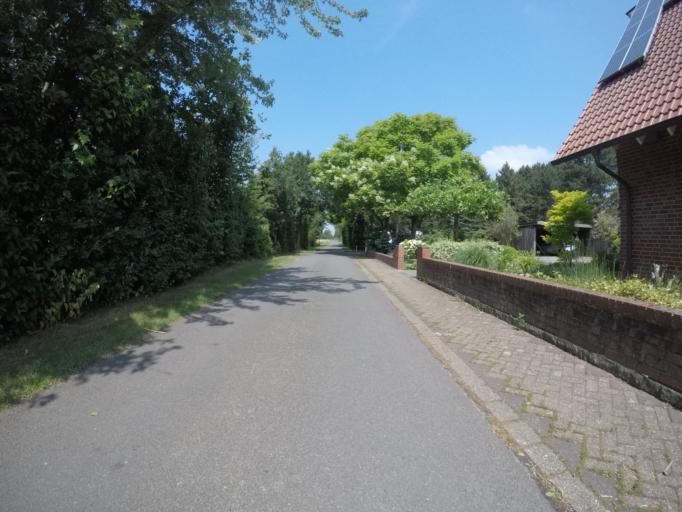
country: DE
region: North Rhine-Westphalia
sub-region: Regierungsbezirk Munster
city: Isselburg
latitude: 51.8279
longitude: 6.5229
